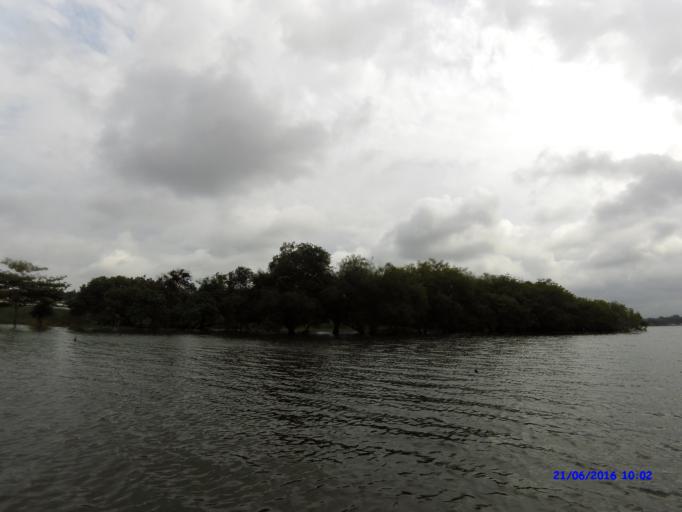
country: BJ
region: Mono
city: Come
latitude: 6.4533
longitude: 1.9248
